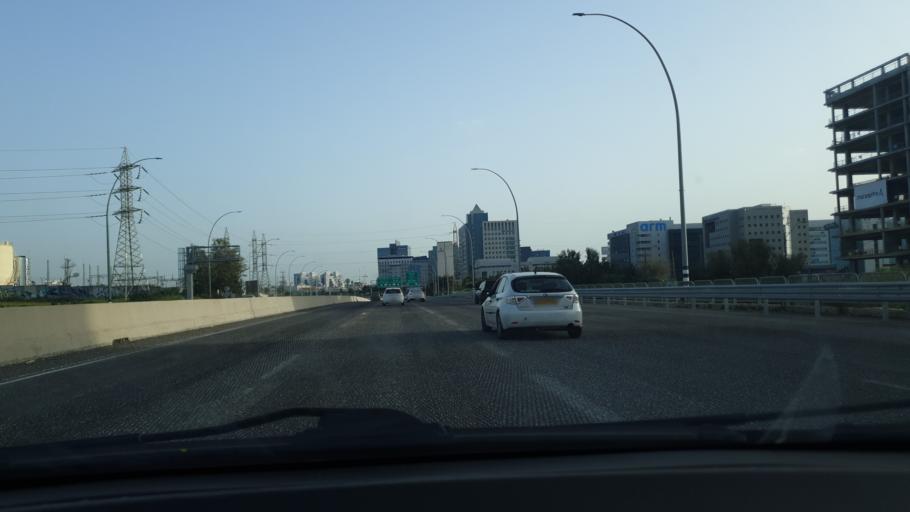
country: IL
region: Central District
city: Ra'anana
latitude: 32.2017
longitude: 34.8844
